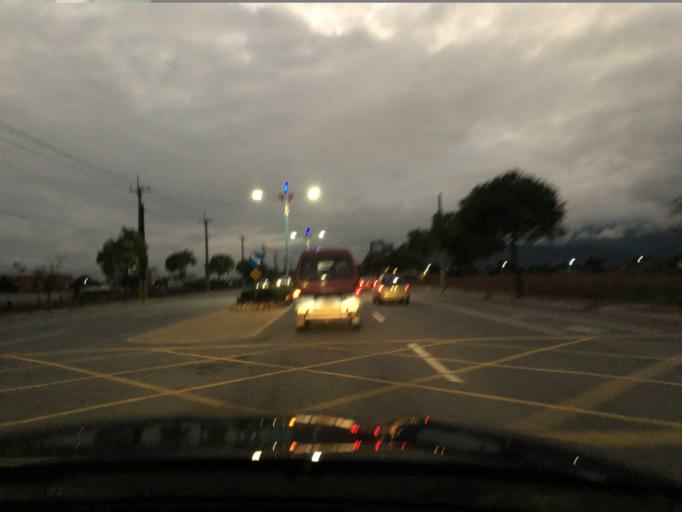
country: TW
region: Taiwan
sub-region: Hualien
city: Hualian
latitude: 23.9674
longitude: 121.5688
